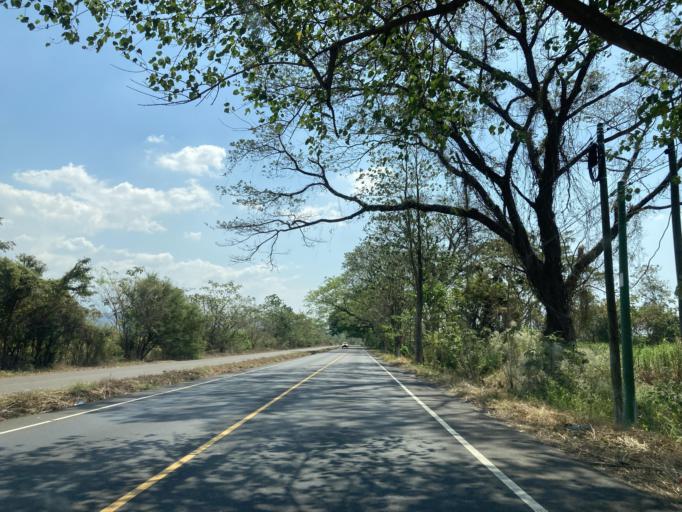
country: GT
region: Escuintla
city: Guanagazapa
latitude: 14.1774
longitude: -90.6846
